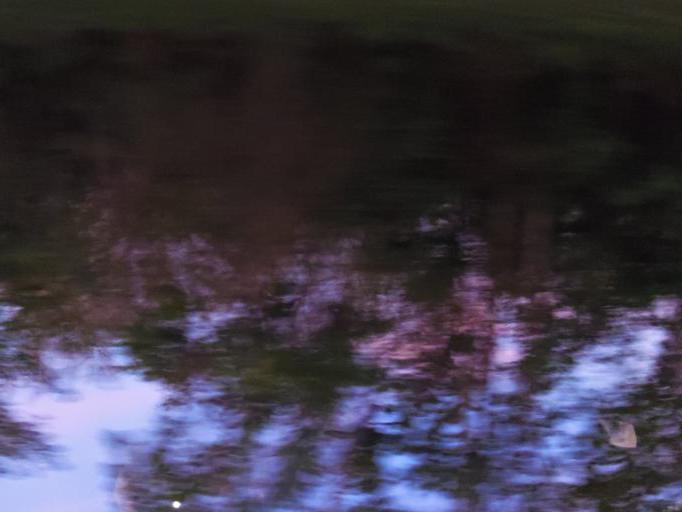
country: US
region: Florida
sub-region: Volusia County
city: De Leon Springs
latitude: 29.1684
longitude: -81.2998
